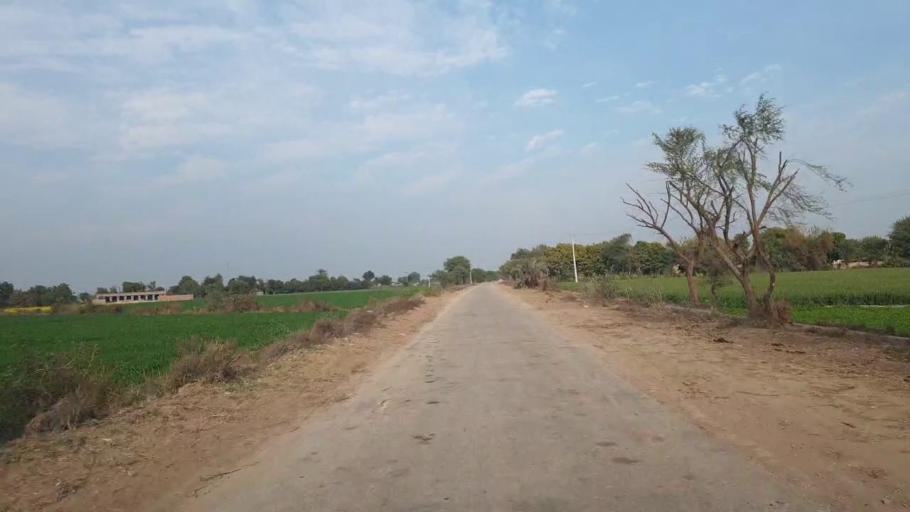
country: PK
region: Sindh
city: Shahdadpur
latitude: 26.0478
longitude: 68.5651
